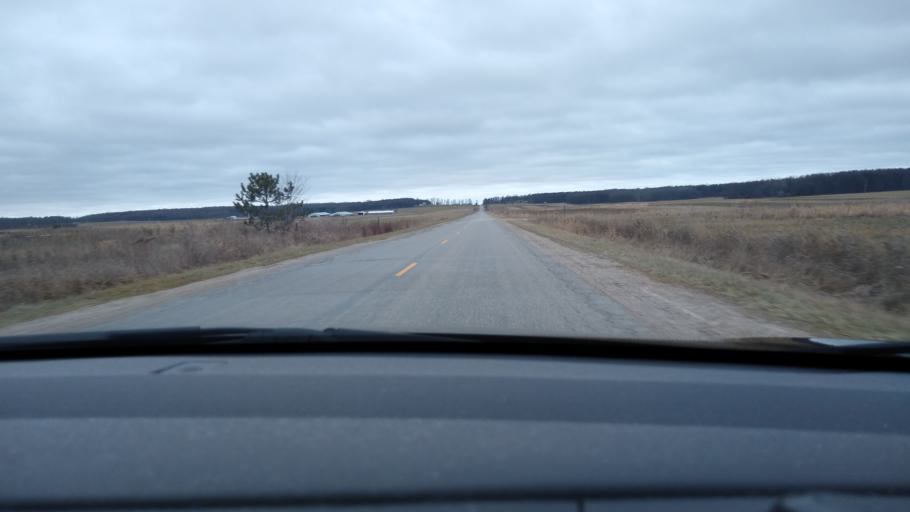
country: US
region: Michigan
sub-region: Missaukee County
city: Lake City
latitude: 44.3070
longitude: -85.0545
